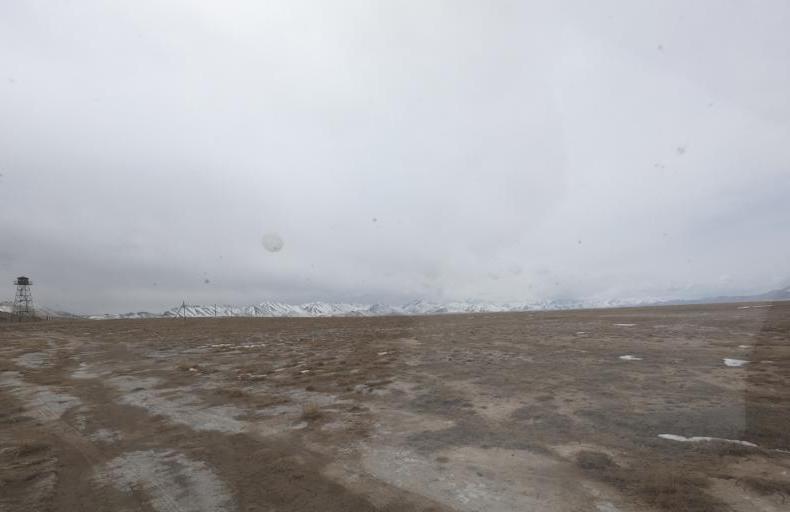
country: KG
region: Naryn
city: At-Bashi
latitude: 40.6461
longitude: 75.4312
